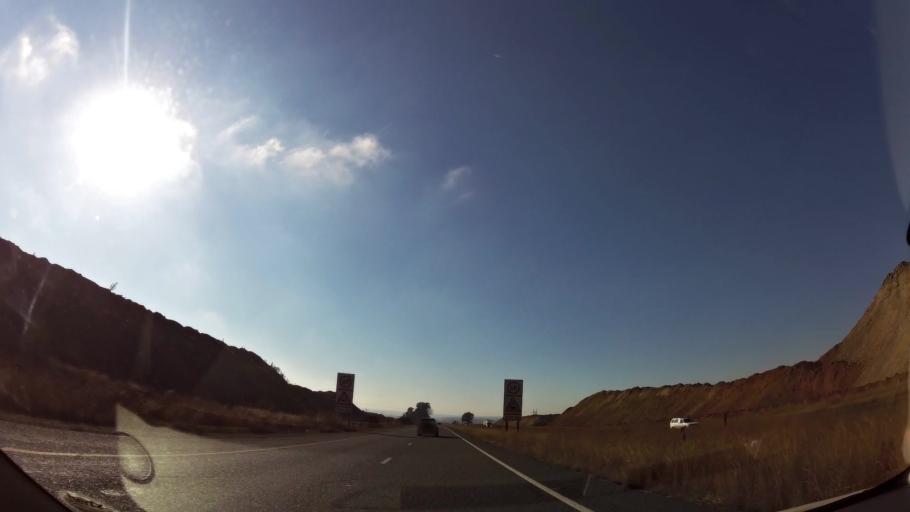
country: ZA
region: Mpumalanga
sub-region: Nkangala District Municipality
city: Witbank
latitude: -26.0179
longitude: 28.9736
